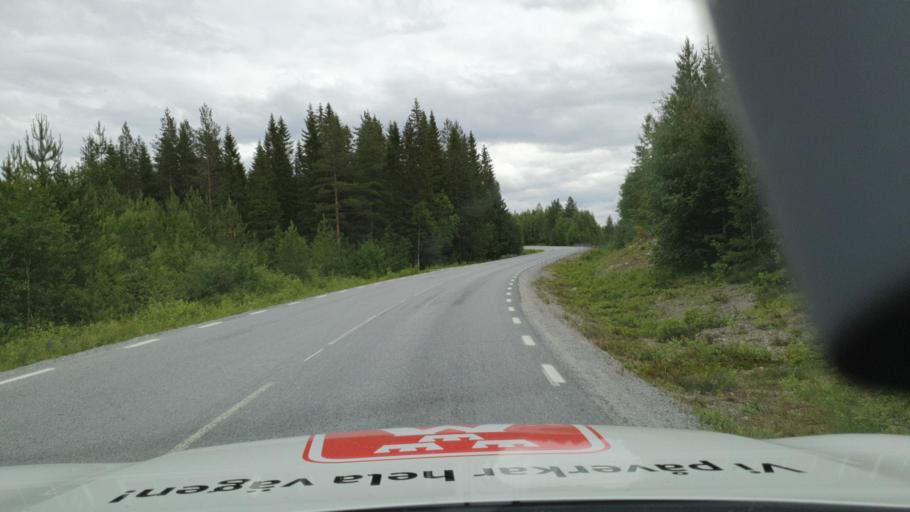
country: SE
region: Vaesterbotten
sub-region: Bjurholms Kommun
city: Bjurholm
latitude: 63.8837
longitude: 19.0284
